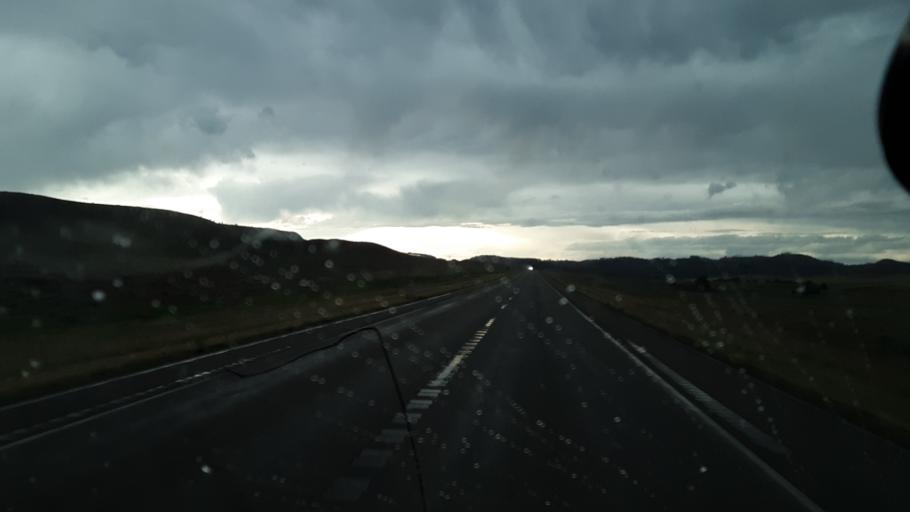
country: US
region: Montana
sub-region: Powder River County
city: Broadus
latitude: 45.5424
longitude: -105.8315
